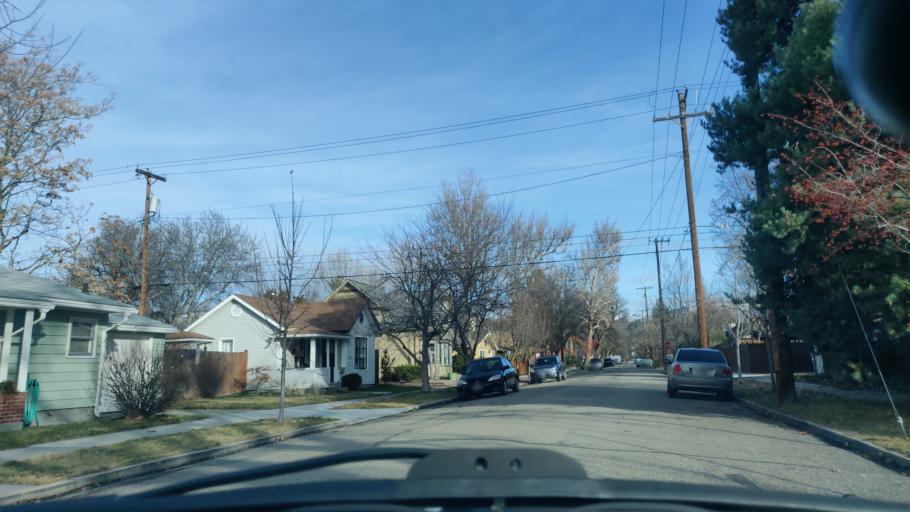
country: US
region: Idaho
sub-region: Ada County
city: Boise
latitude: 43.6284
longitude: -116.2057
